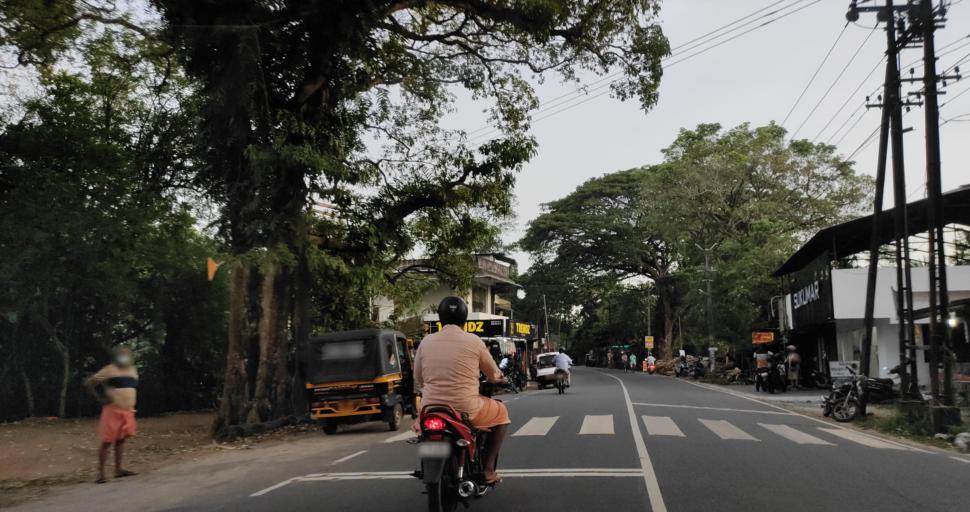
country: IN
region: Kerala
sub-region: Alappuzha
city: Shertallai
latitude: 9.6419
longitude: 76.3704
